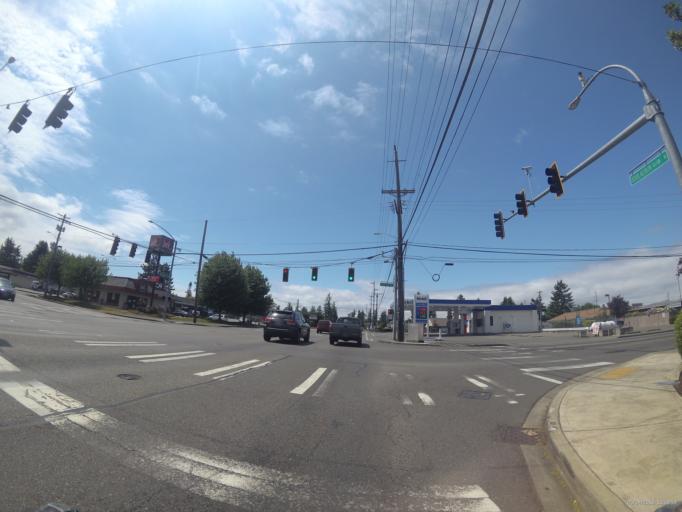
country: US
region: Washington
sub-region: Pierce County
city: Lakewood
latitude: 47.1800
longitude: -122.5474
